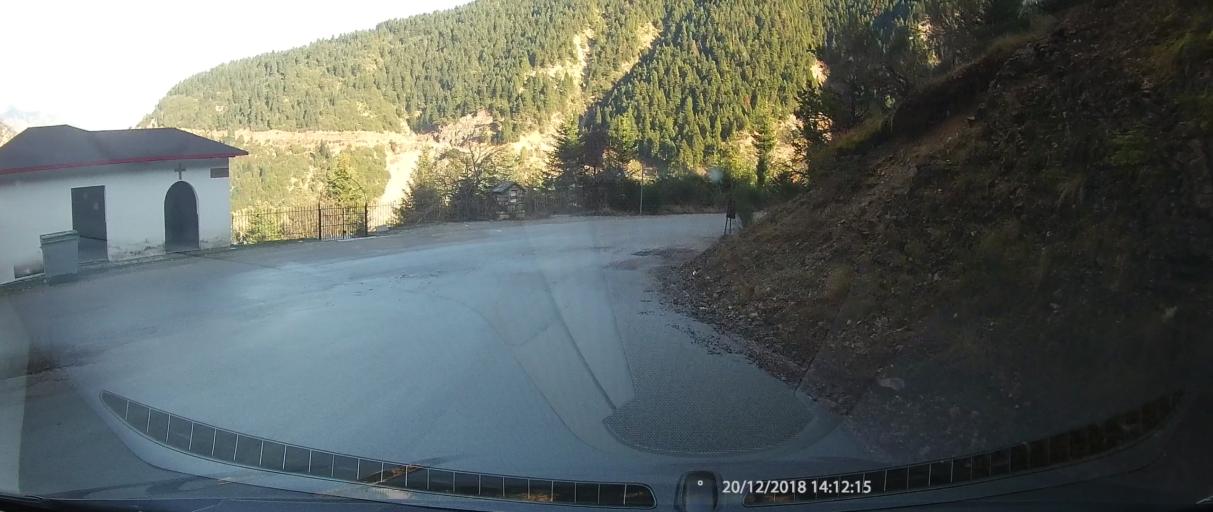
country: GR
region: West Greece
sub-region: Nomos Aitolias kai Akarnanias
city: Thermo
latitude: 38.7379
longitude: 21.6536
